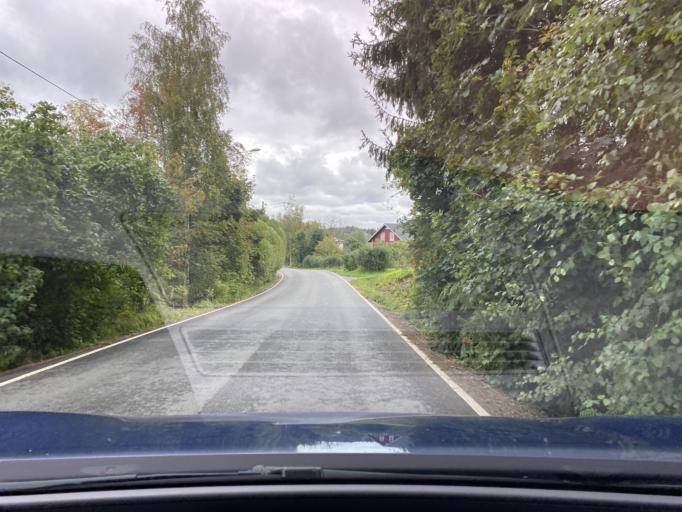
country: FI
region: Pirkanmaa
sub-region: Lounais-Pirkanmaa
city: Punkalaidun
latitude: 61.1671
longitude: 23.1816
